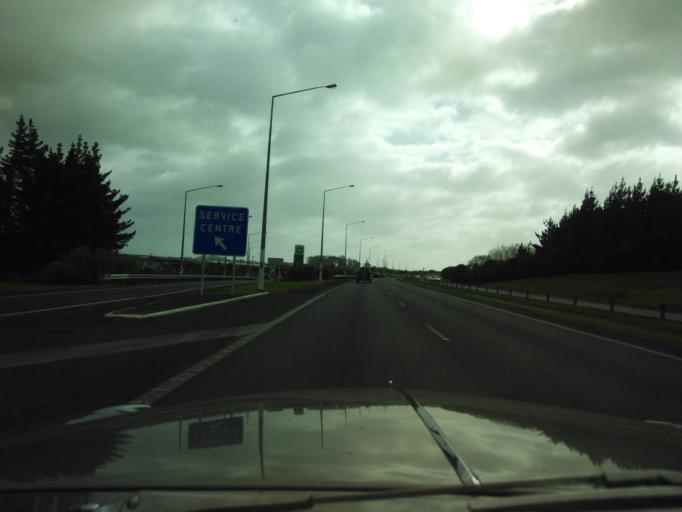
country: NZ
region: Auckland
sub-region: Auckland
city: Rothesay Bay
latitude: -36.6616
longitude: 174.6697
